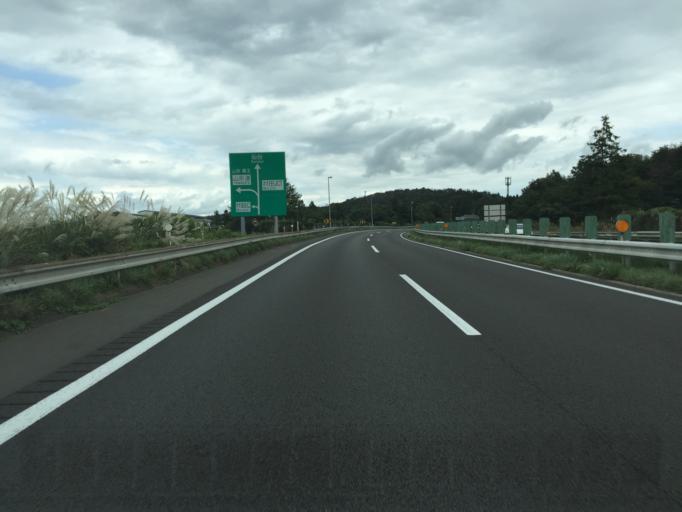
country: JP
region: Miyagi
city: Okawara
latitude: 38.1143
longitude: 140.6984
